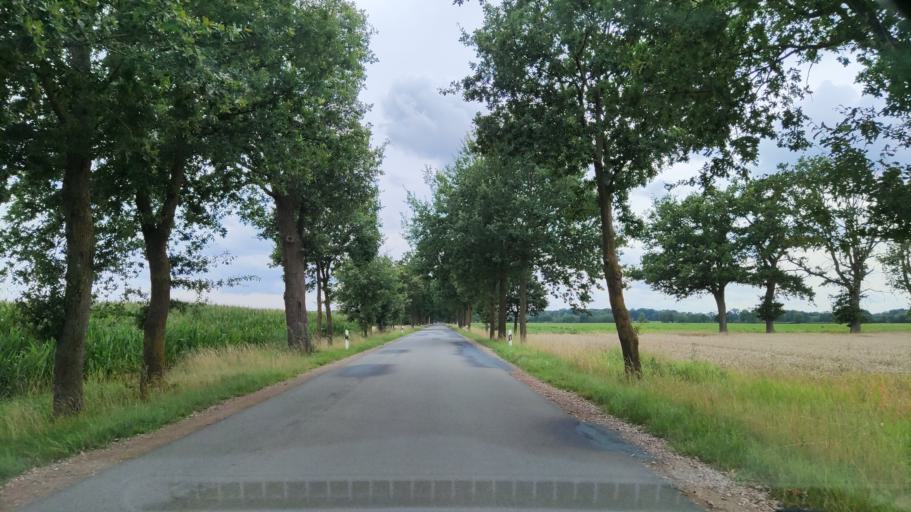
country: DE
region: Lower Saxony
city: Dannenberg
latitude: 53.0794
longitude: 11.1339
